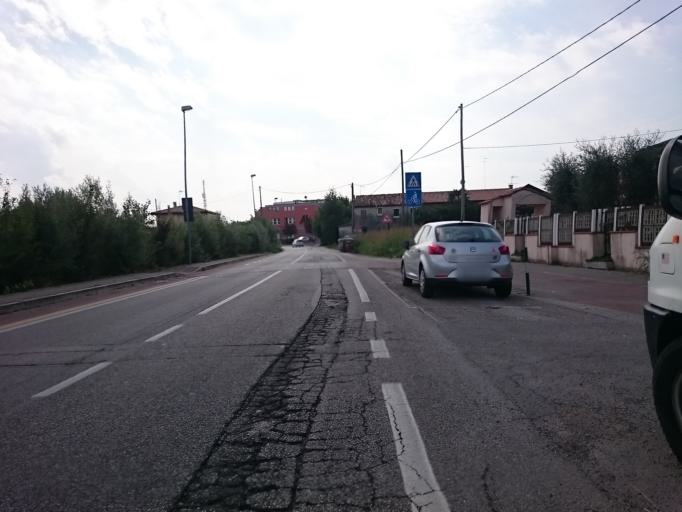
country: IT
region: Veneto
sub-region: Provincia di Padova
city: Padova
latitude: 45.3978
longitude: 11.9098
